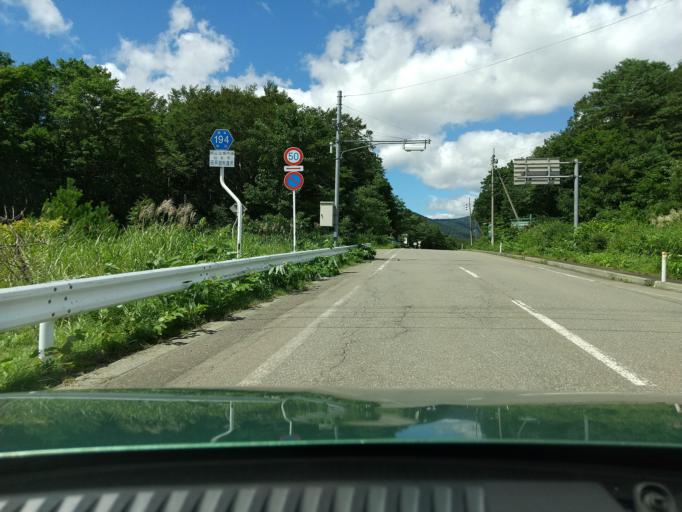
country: JP
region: Iwate
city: Shizukuishi
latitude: 39.7697
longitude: 140.7638
